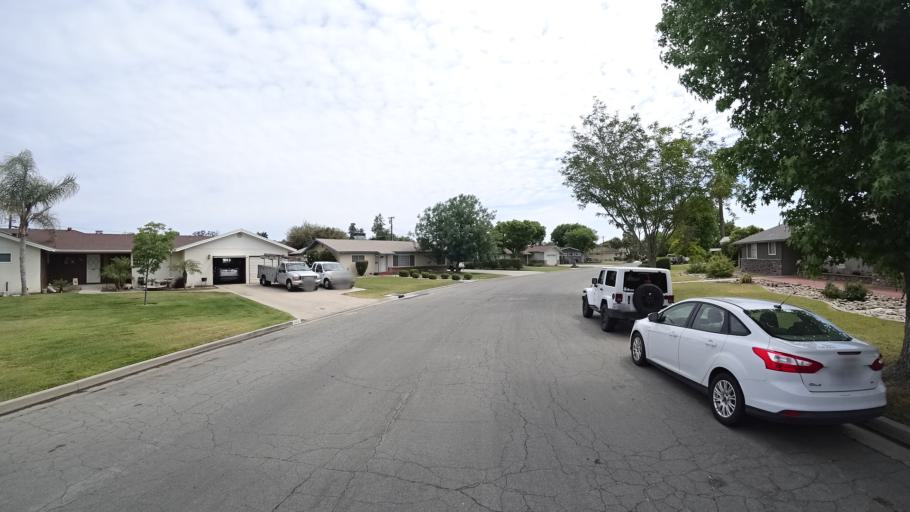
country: US
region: California
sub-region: Kings County
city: Hanford
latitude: 36.3545
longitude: -119.6442
